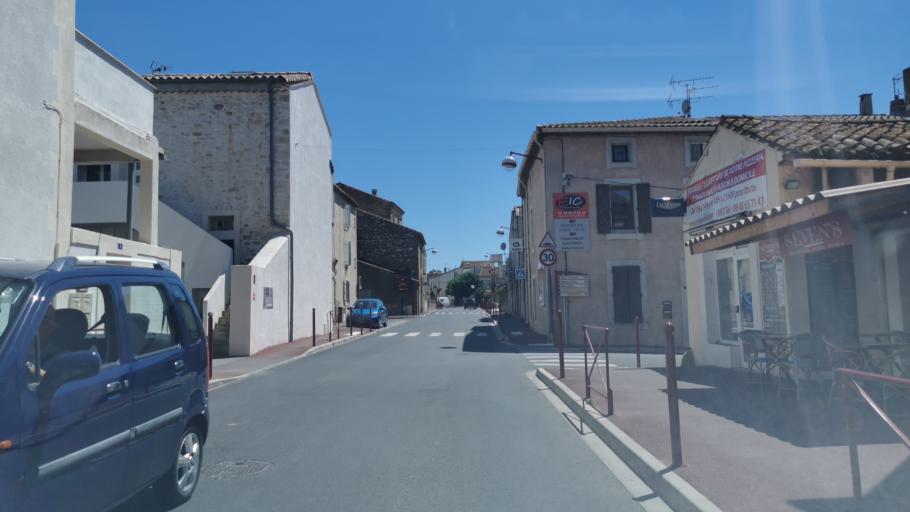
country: FR
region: Languedoc-Roussillon
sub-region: Departement de l'Aude
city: Vinassan
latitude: 43.2035
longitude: 3.0746
